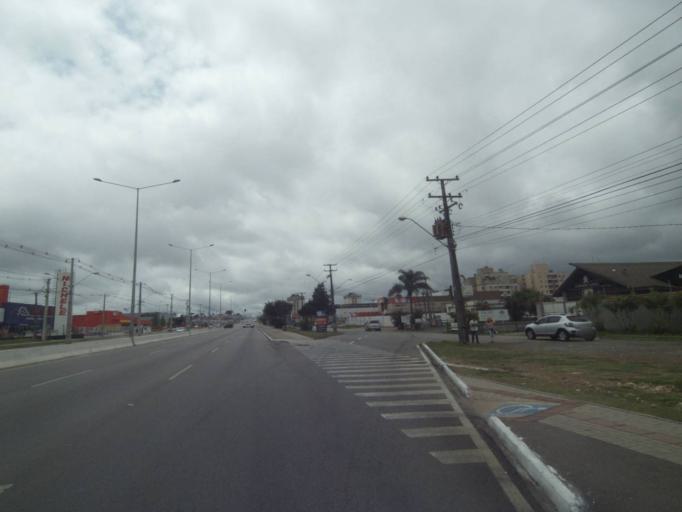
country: BR
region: Parana
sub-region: Pinhais
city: Pinhais
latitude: -25.4317
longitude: -49.2005
